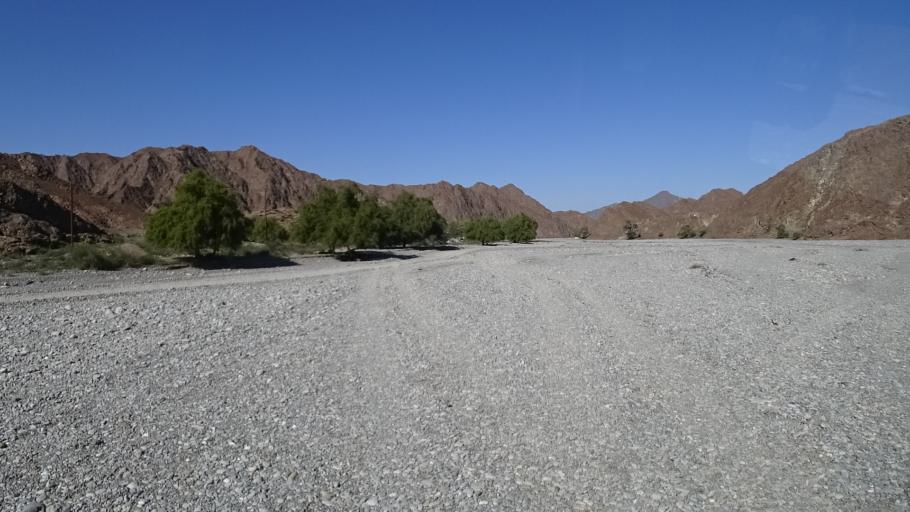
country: OM
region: Al Batinah
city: Bayt al `Awabi
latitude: 23.3918
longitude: 57.6625
